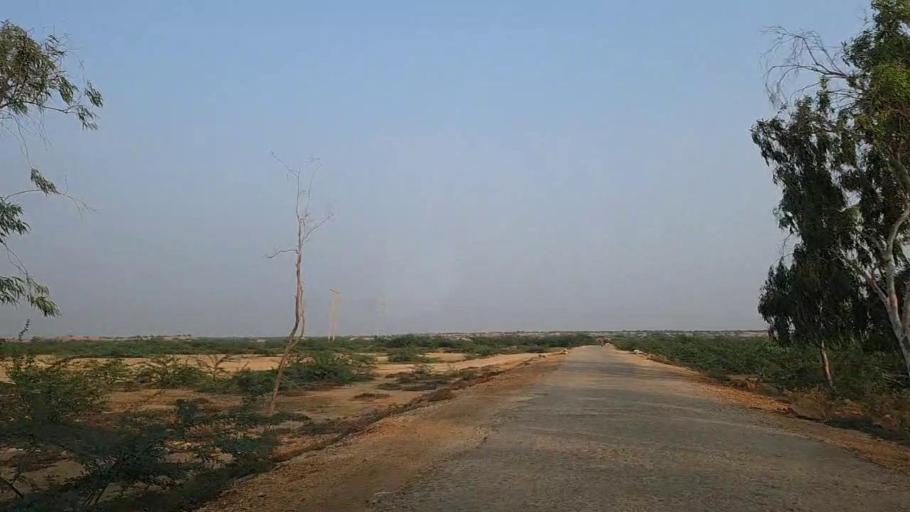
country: PK
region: Sindh
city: Thatta
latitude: 24.6899
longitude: 67.8485
